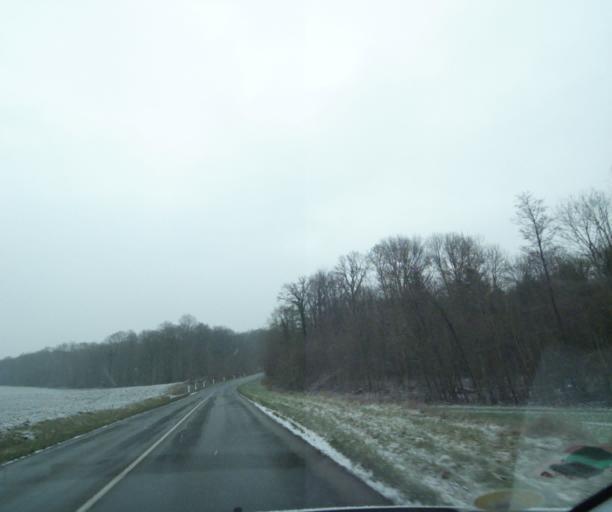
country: FR
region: Champagne-Ardenne
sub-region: Departement de la Haute-Marne
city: Wassy
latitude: 48.4775
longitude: 5.0112
